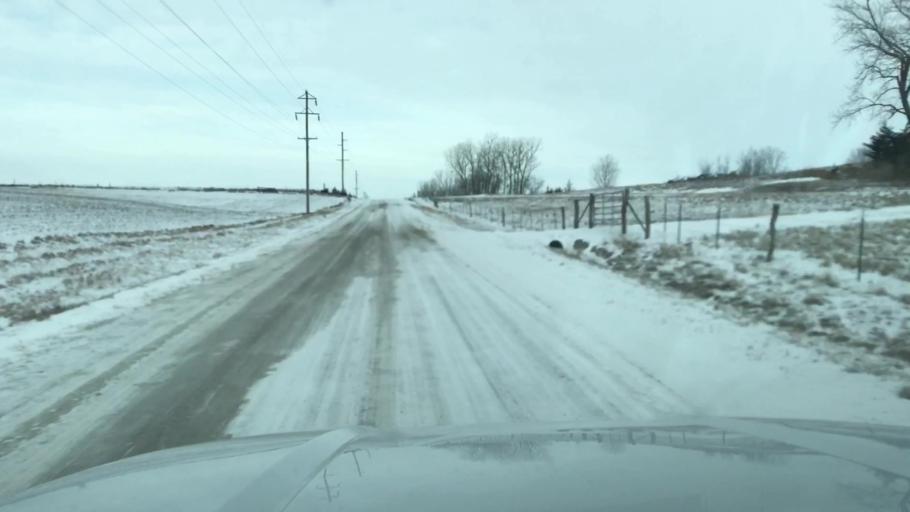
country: US
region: Missouri
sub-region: Holt County
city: Oregon
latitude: 40.1301
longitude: -95.0588
